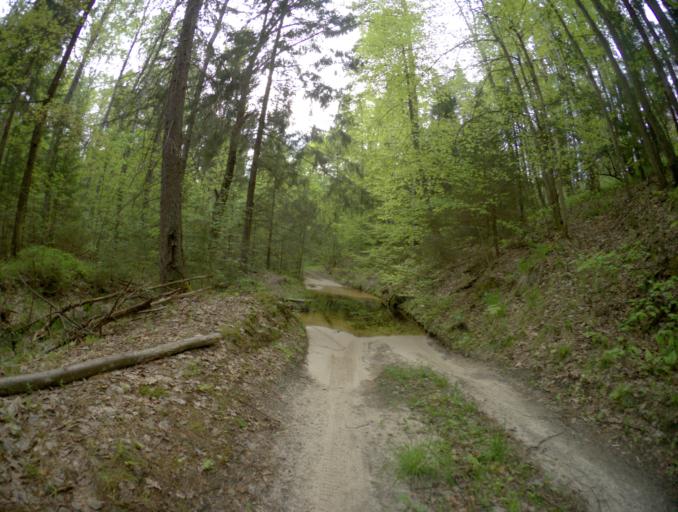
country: RU
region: Rjazan
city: Gus'-Zheleznyy
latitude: 55.1901
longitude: 41.0714
